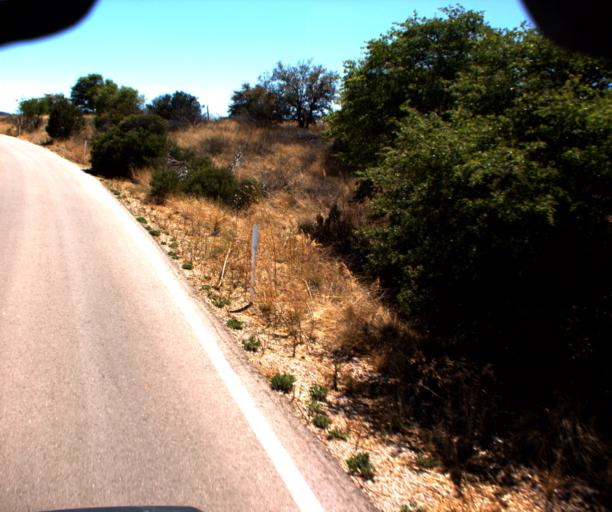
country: US
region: Arizona
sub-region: Cochise County
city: Huachuca City
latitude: 31.5204
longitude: -110.4994
